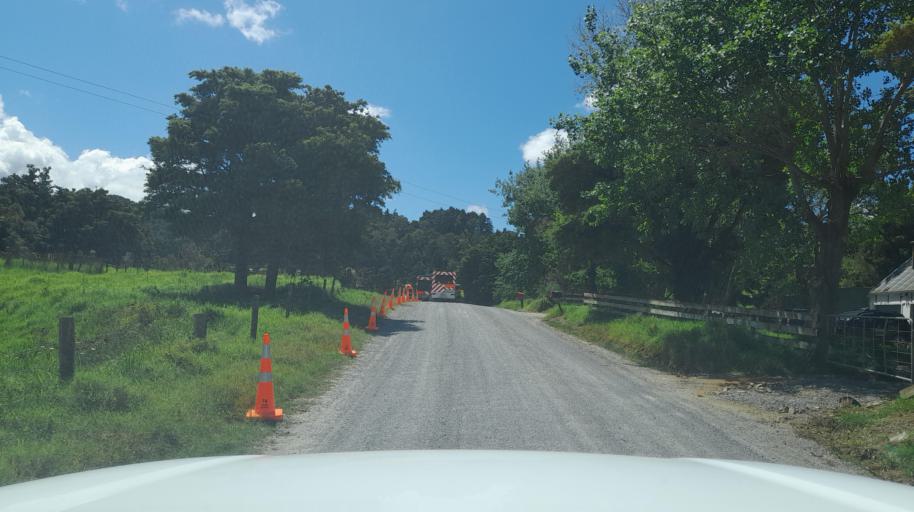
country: NZ
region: Northland
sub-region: Far North District
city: Kaitaia
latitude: -35.1109
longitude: 173.3954
